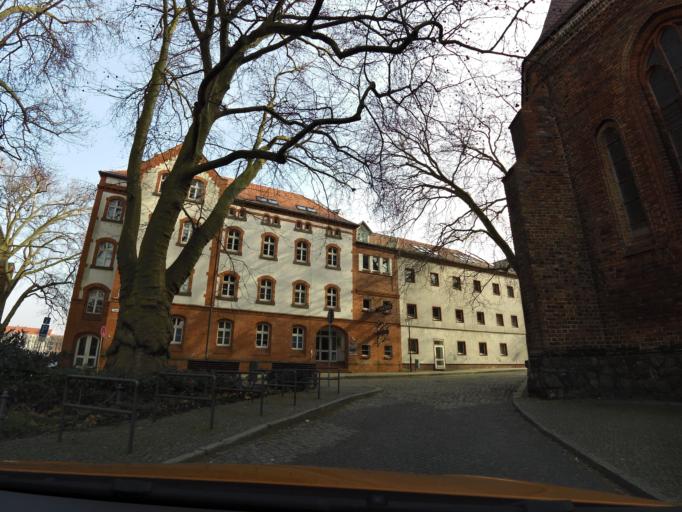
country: DE
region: Brandenburg
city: Frankfurt (Oder)
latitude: 52.3488
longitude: 14.5525
